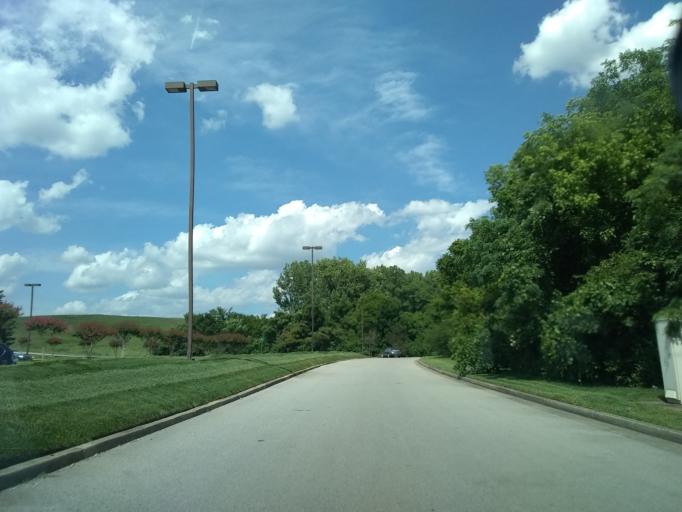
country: US
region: Tennessee
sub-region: Davidson County
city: Nashville
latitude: 36.1361
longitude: -86.6984
